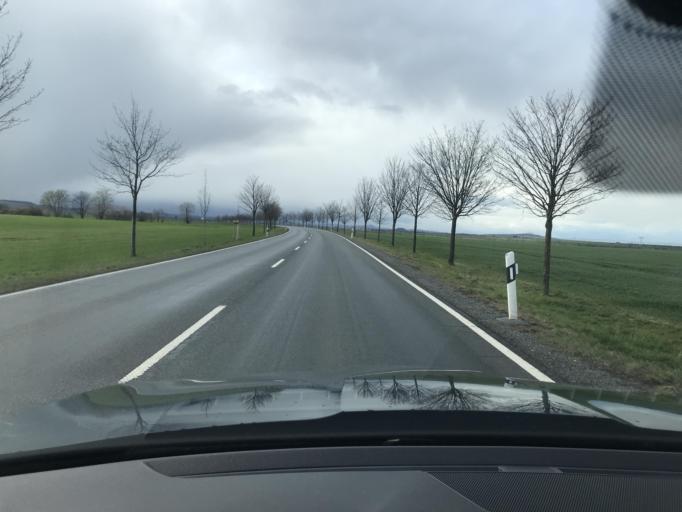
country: DE
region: Saxony-Anhalt
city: Gatersleben
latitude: 51.7857
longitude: 11.2678
